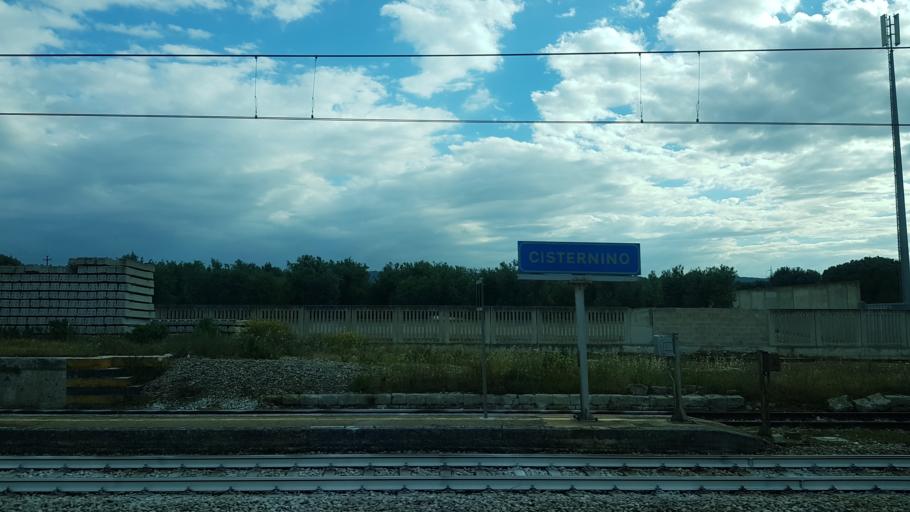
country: IT
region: Apulia
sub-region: Provincia di Brindisi
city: Pezze di Greco
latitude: 40.8171
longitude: 17.4558
